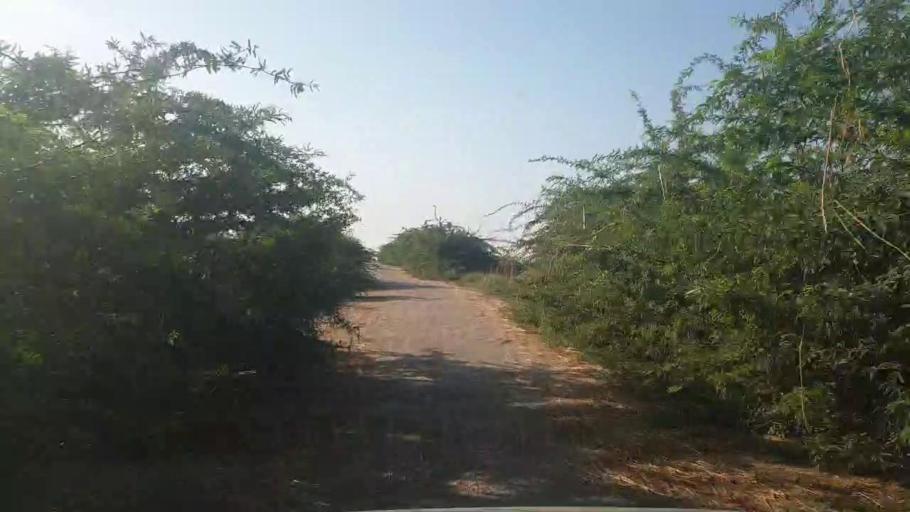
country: PK
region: Sindh
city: Tando Bago
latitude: 24.7415
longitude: 68.9305
